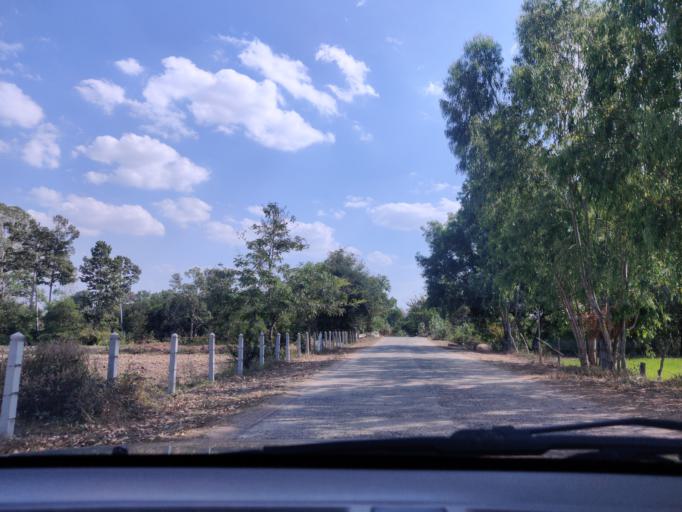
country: TH
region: Sisaket
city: Si Sa Ket
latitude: 15.0701
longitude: 104.3493
